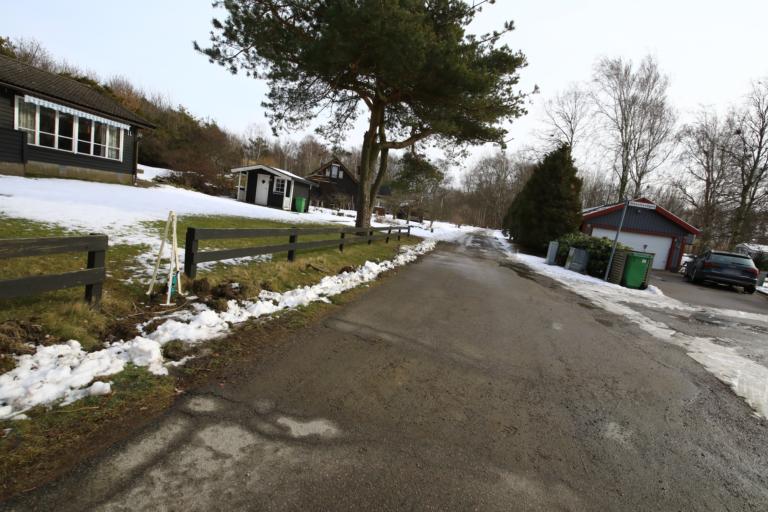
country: SE
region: Halland
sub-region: Kungsbacka Kommun
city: Frillesas
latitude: 57.2162
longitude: 12.1611
